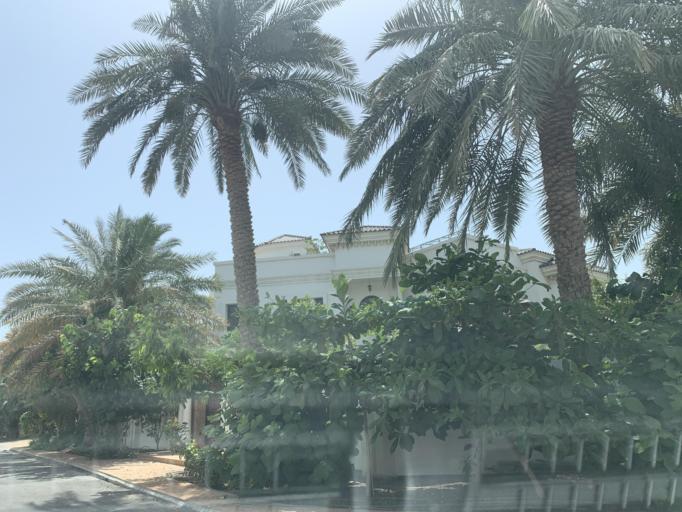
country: BH
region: Northern
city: Sitrah
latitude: 26.1558
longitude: 50.5838
